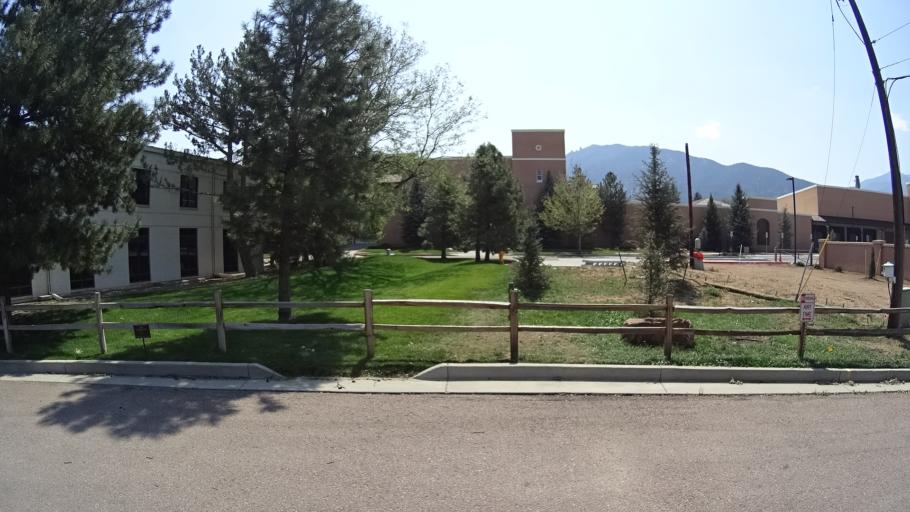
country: US
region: Colorado
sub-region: El Paso County
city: Colorado Springs
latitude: 38.7938
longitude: -104.8493
